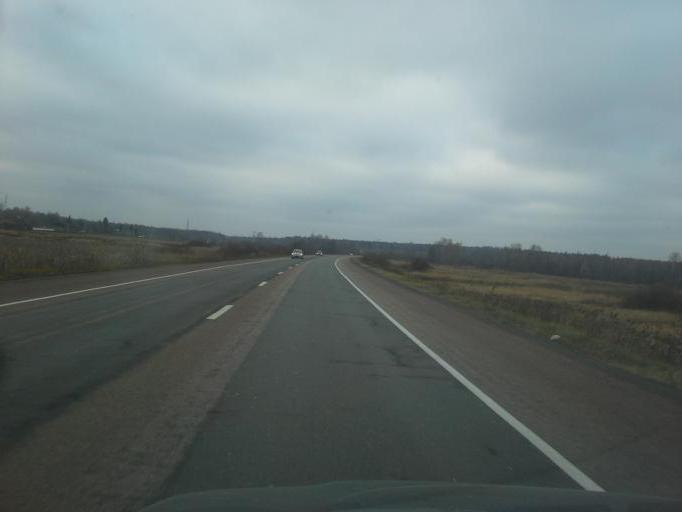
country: RU
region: Moskovskaya
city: Solnechnogorsk
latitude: 56.1482
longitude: 36.9330
